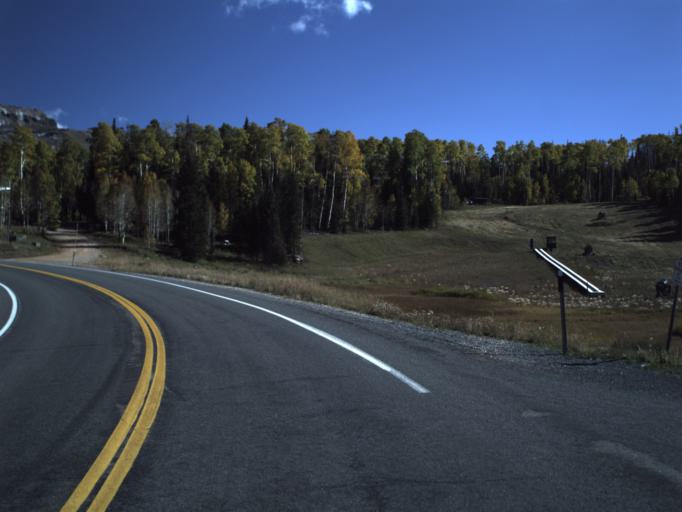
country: US
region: Utah
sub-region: Iron County
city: Parowan
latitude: 37.7034
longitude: -112.8487
